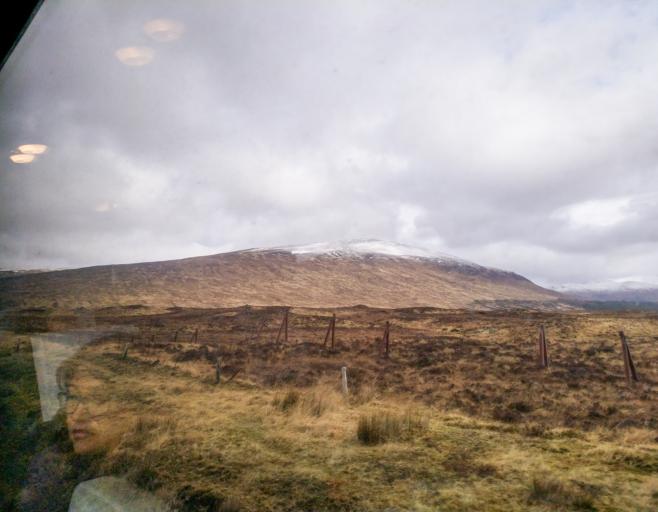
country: GB
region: Scotland
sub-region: Highland
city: Spean Bridge
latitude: 56.7572
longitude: -4.6865
